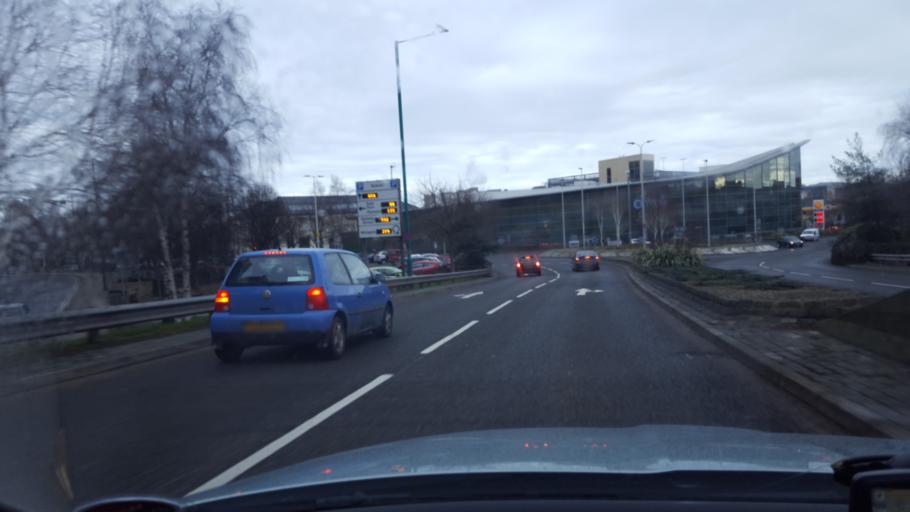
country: GB
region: Scotland
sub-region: Dundee City
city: Dundee
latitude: 56.4646
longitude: -2.9656
